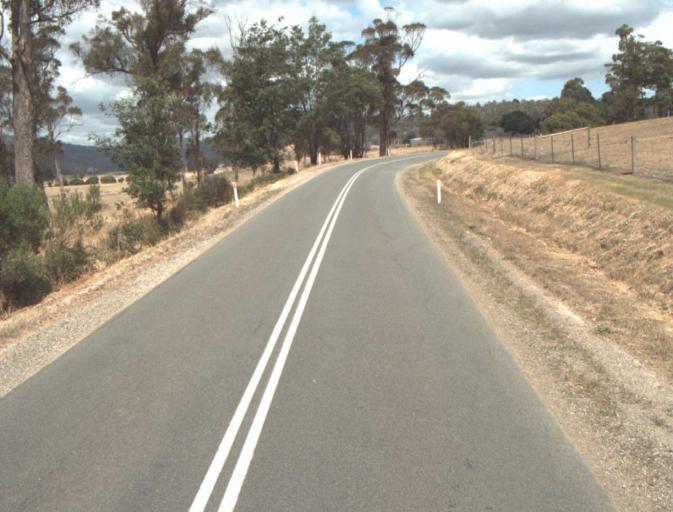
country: AU
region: Tasmania
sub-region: Launceston
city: Mayfield
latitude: -41.2245
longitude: 147.1222
